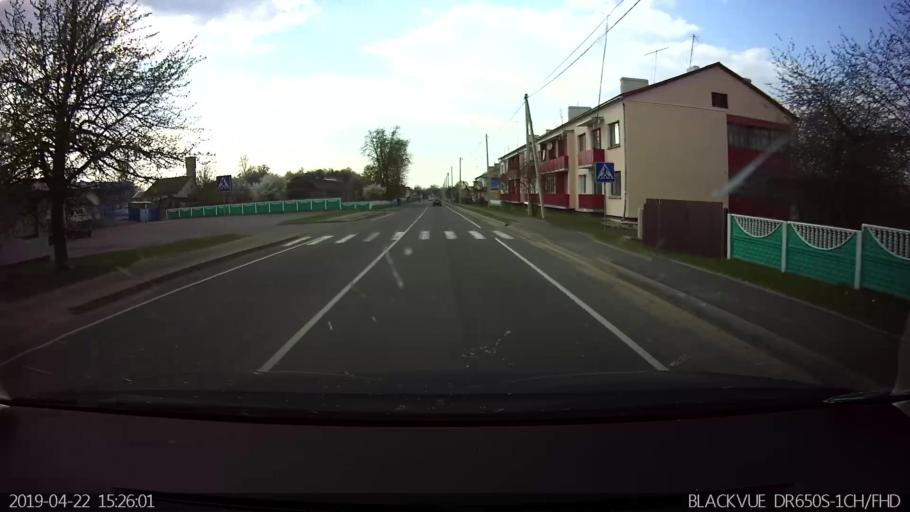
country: BY
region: Brest
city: Vysokaye
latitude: 52.3666
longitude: 23.3878
